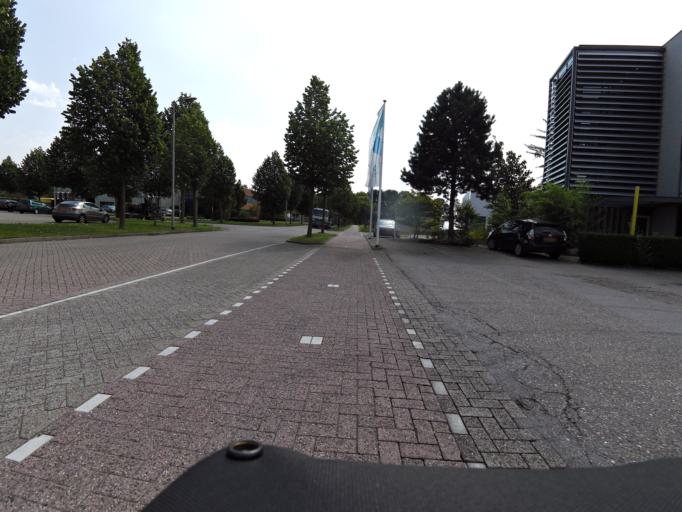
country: NL
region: South Holland
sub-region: Gemeente Oud-Beijerland
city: Oud-Beijerland
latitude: 51.8232
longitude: 4.4375
